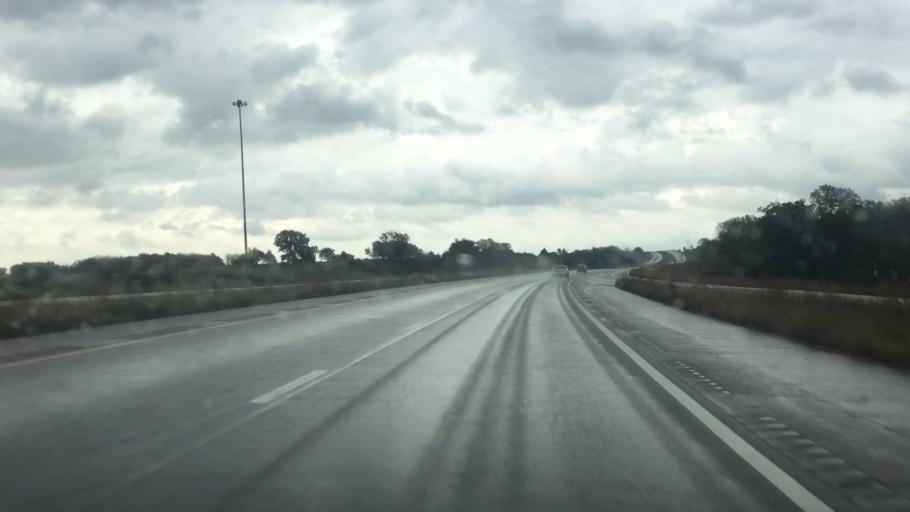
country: US
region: Kansas
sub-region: Miami County
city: Osawatomie
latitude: 38.5122
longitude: -94.9264
